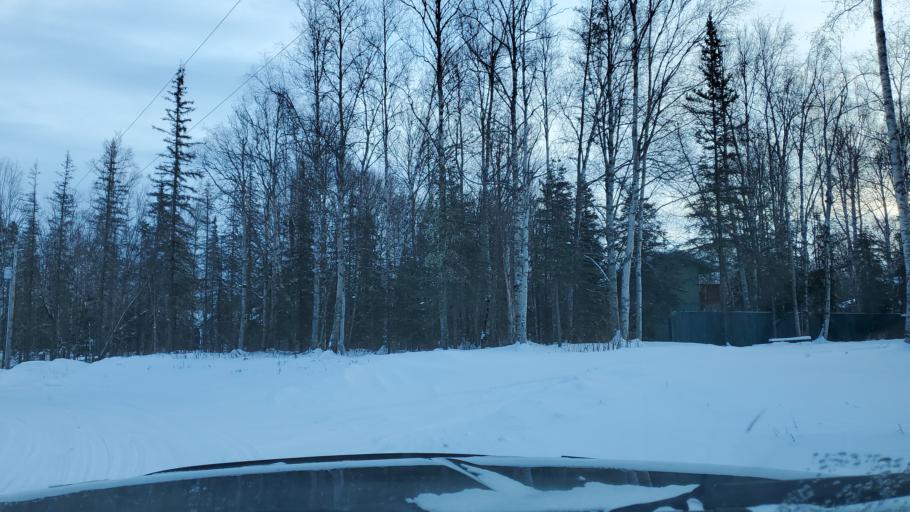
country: US
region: Alaska
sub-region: Matanuska-Susitna Borough
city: Lakes
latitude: 61.6653
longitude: -149.2943
